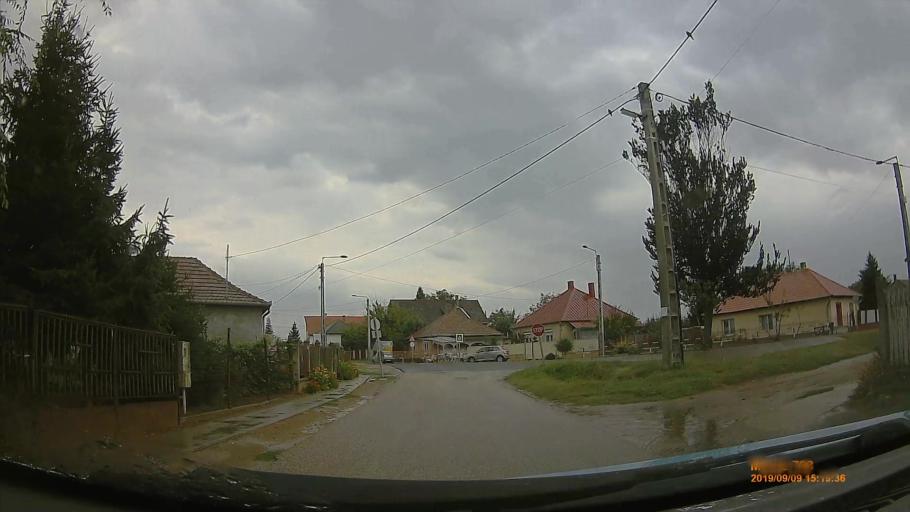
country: HU
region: Szabolcs-Szatmar-Bereg
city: Nyirpazony
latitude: 48.0138
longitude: 21.8315
